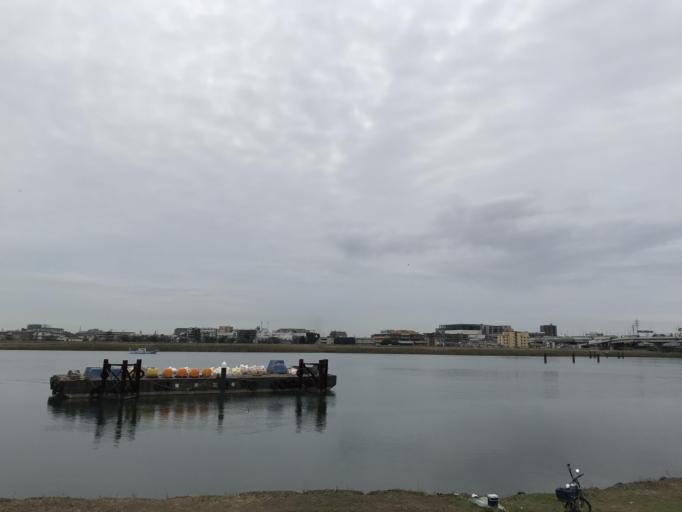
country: JP
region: Kanagawa
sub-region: Kawasaki-shi
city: Kawasaki
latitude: 35.5447
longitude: 139.7458
